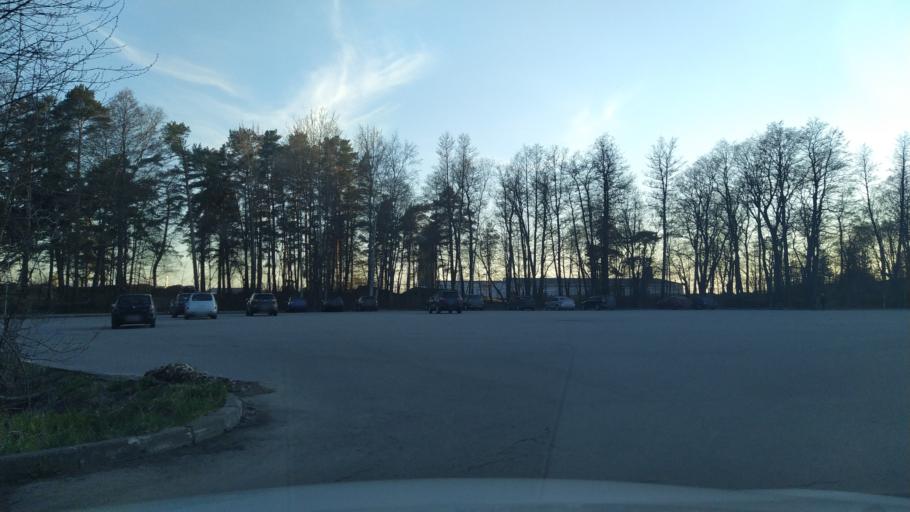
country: RU
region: St.-Petersburg
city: Solnechnoye
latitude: 60.1464
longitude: 29.9280
